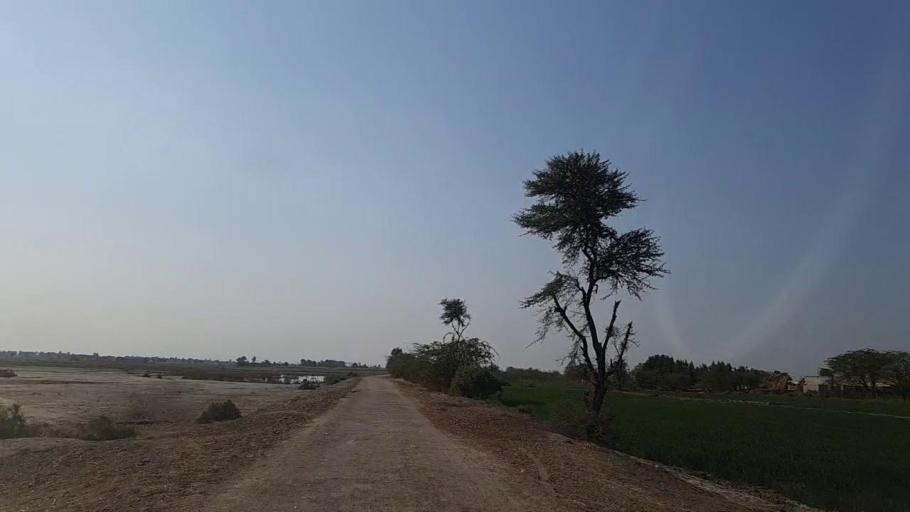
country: PK
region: Sindh
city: Daur
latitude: 26.4366
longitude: 68.2680
